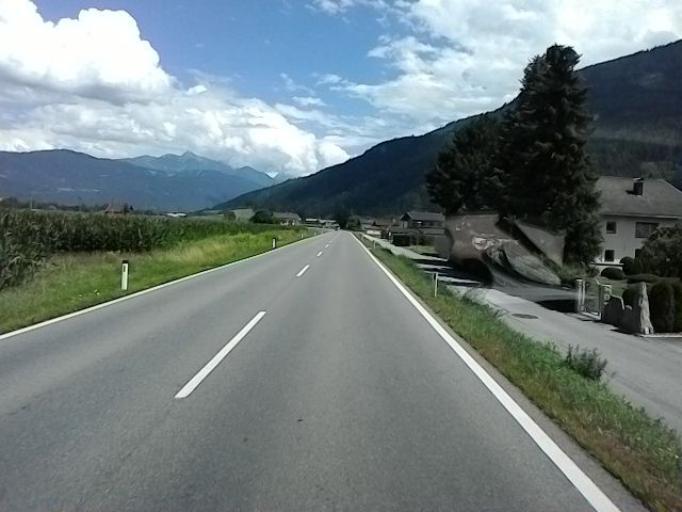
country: AT
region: Tyrol
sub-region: Politischer Bezirk Imst
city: Rietz
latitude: 47.2920
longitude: 11.0351
